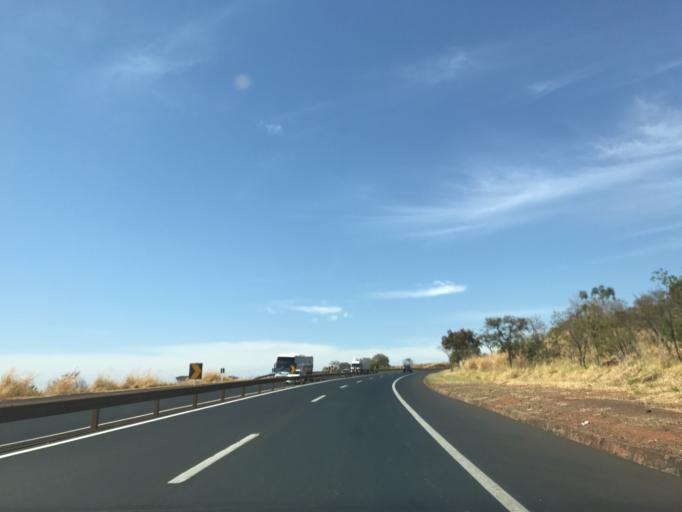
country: BR
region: Minas Gerais
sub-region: Monte Alegre De Minas
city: Monte Alegre de Minas
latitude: -18.7977
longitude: -49.0818
